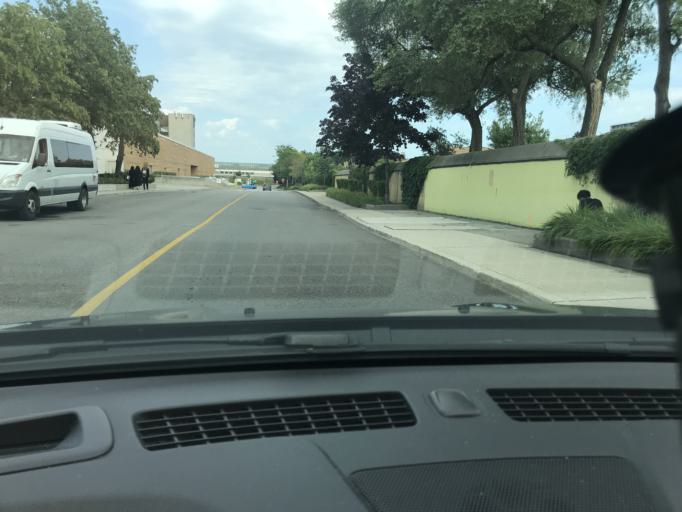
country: CA
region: Ontario
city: Toronto
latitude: 43.7241
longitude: -79.4518
